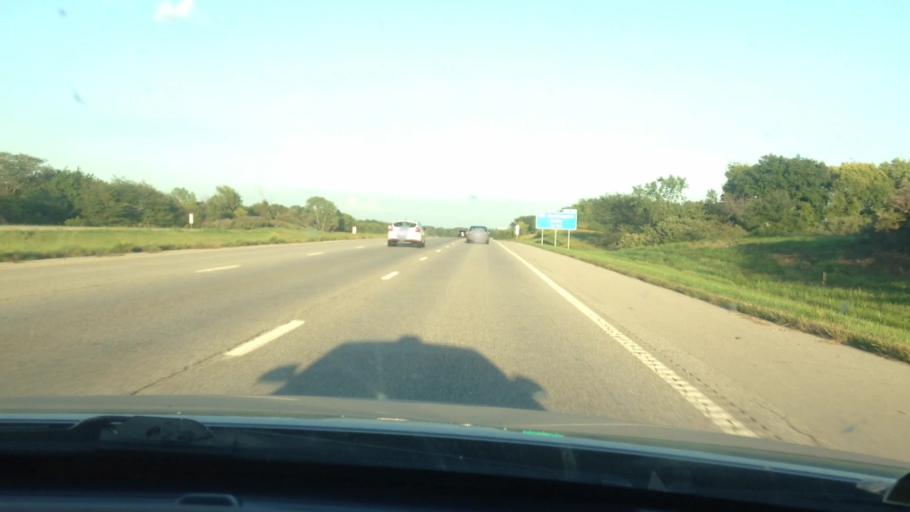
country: US
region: Missouri
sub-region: Clay County
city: Smithville
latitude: 39.3075
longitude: -94.6197
